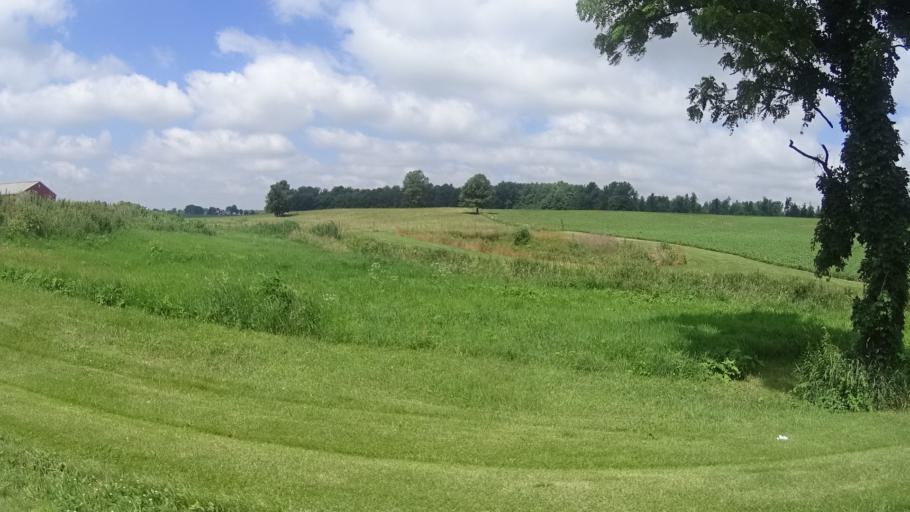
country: US
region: Ohio
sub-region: Huron County
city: Wakeman
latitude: 41.3094
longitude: -82.3870
